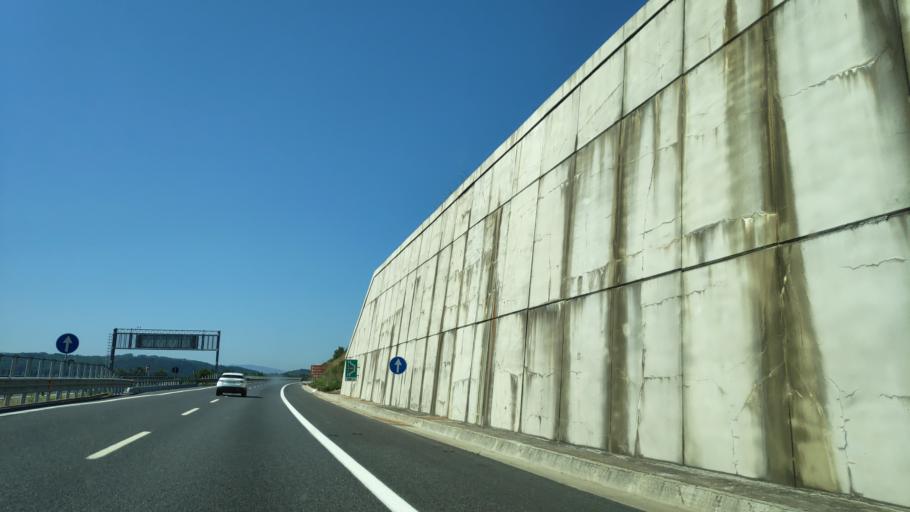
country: IT
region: Calabria
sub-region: Provincia di Reggio Calabria
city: Seminara
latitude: 38.3470
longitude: 15.8696
